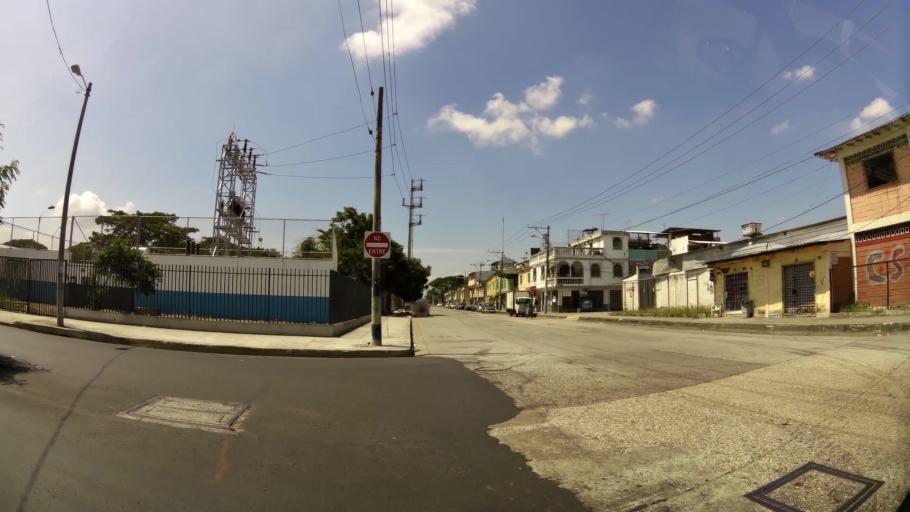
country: EC
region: Guayas
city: Guayaquil
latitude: -2.2357
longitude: -79.8991
